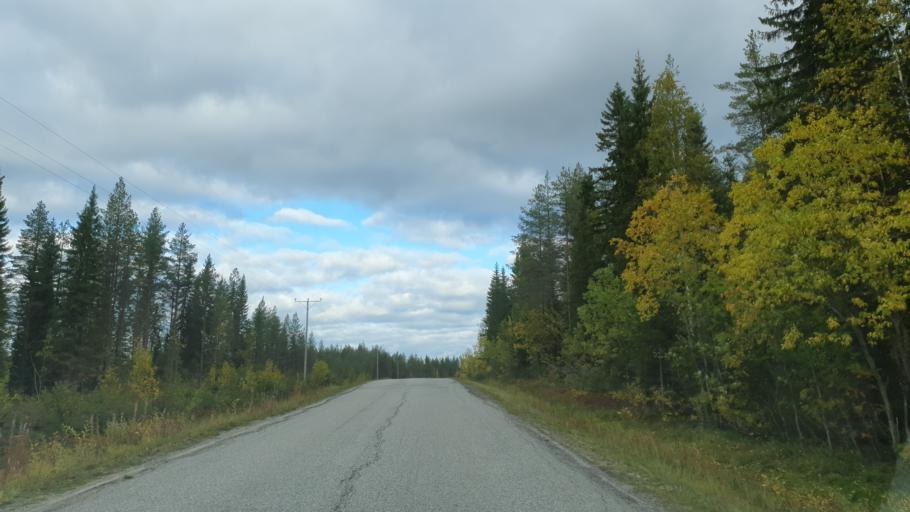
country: FI
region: Kainuu
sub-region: Kehys-Kainuu
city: Kuhmo
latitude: 63.9498
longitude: 29.8233
